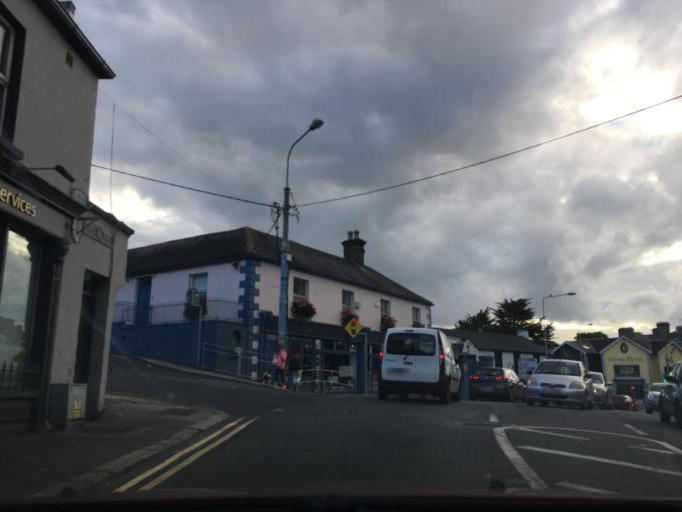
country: IE
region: Leinster
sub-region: Wicklow
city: Wicklow
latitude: 52.9808
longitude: -6.0456
